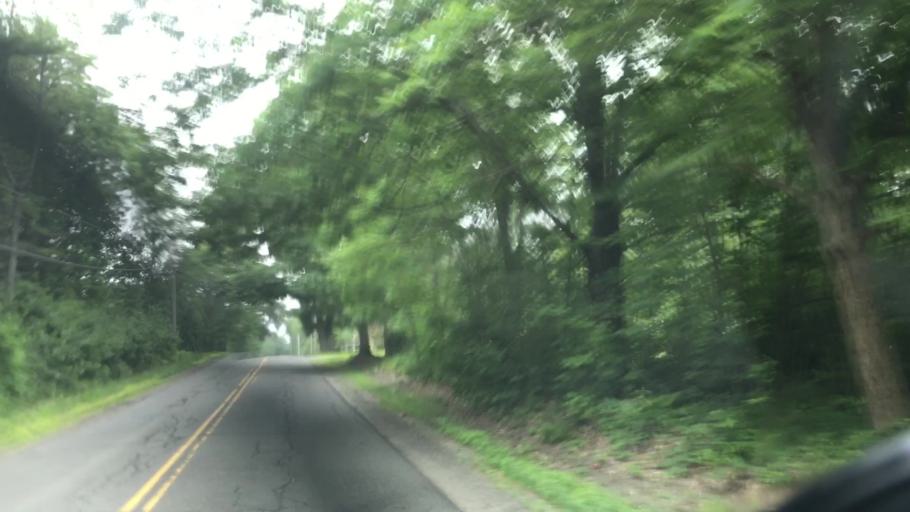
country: US
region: Maine
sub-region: Penobscot County
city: Orono
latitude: 44.8858
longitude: -68.7079
